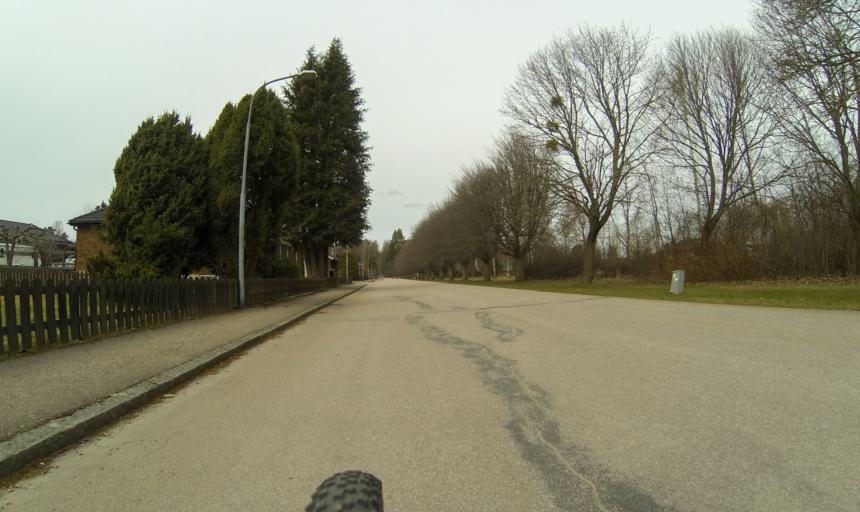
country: SE
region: Vaestmanland
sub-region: Vasteras
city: Vasteras
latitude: 59.5946
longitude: 16.6102
